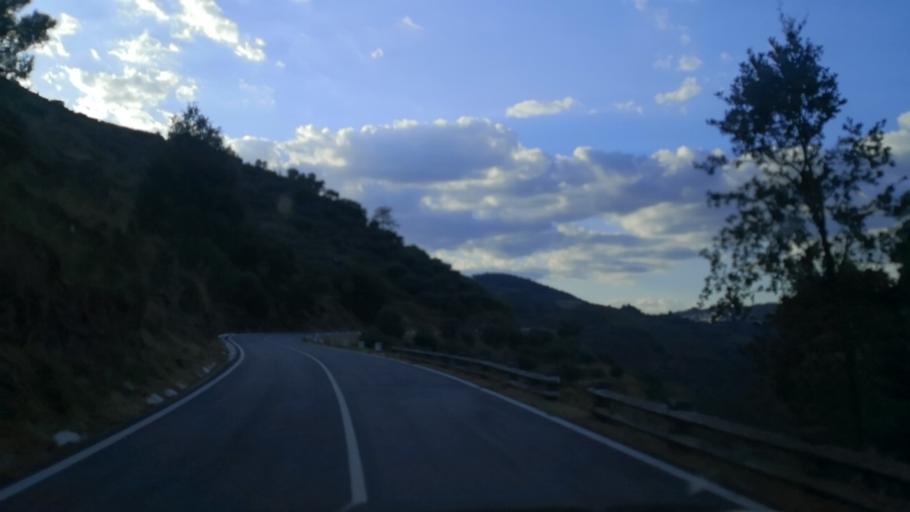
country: PT
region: Viseu
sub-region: Sao Joao da Pesqueira
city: Sao Joao da Pesqueira
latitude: 41.2273
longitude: -7.4243
